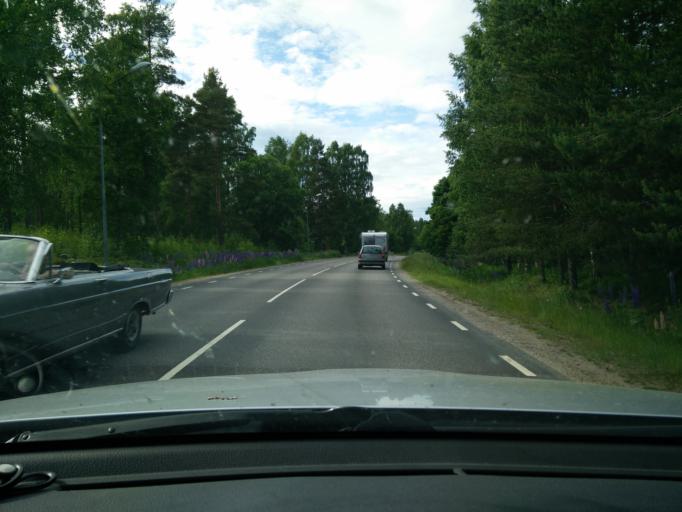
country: SE
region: Gaevleborg
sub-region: Nordanstigs Kommun
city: Bergsjoe
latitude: 61.9723
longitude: 17.0542
